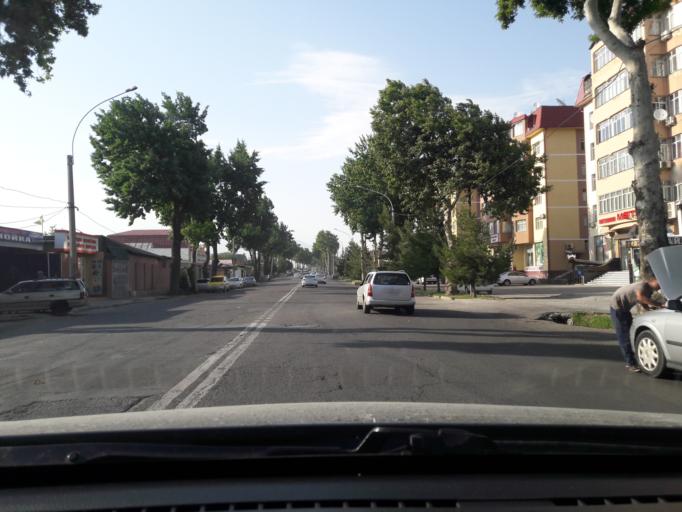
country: TJ
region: Dushanbe
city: Dushanbe
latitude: 38.5426
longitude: 68.7717
